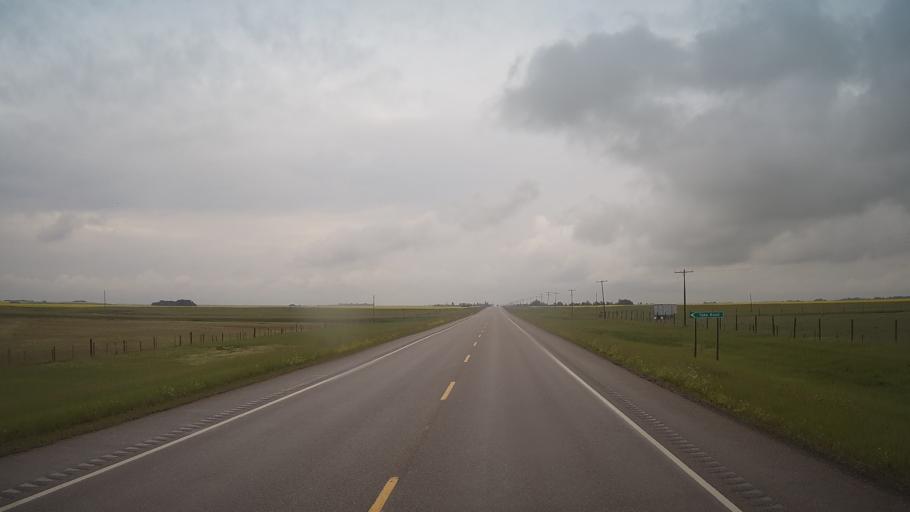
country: CA
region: Saskatchewan
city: Unity
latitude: 52.4349
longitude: -108.9983
